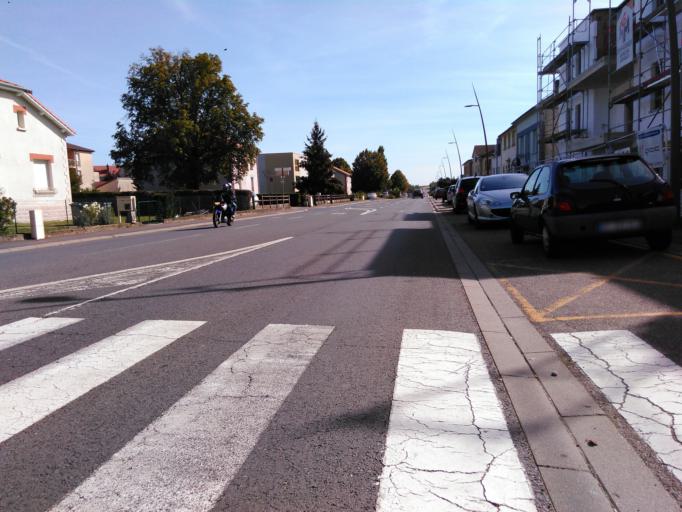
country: FR
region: Lorraine
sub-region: Departement de la Moselle
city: Hettange-Grande
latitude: 49.4009
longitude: 6.1598
